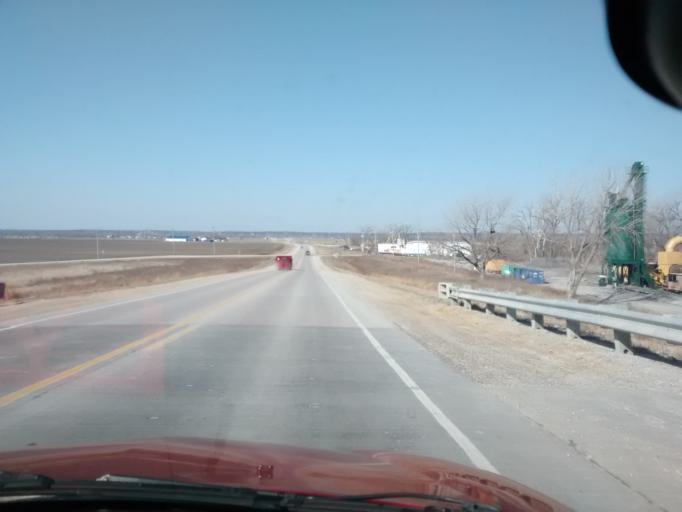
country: US
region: Iowa
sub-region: Pottawattamie County
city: Carter Lake
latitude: 41.3596
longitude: -95.8816
